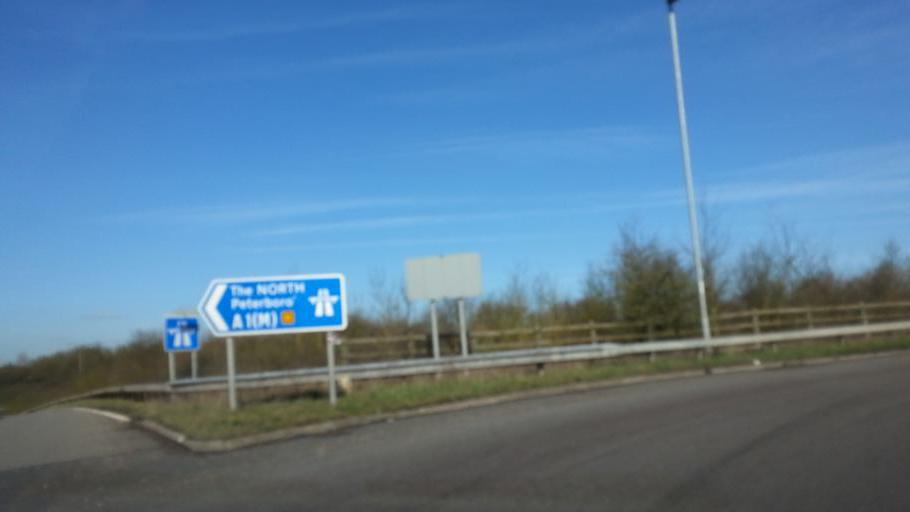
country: GB
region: England
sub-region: Cambridgeshire
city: Great Stukeley
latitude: 52.3727
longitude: -0.2454
